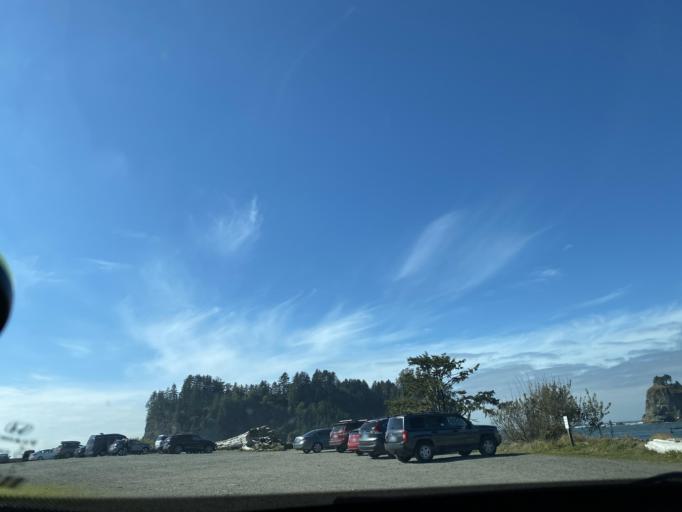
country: US
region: Washington
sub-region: Clallam County
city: Forks
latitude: 47.9088
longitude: -124.6392
